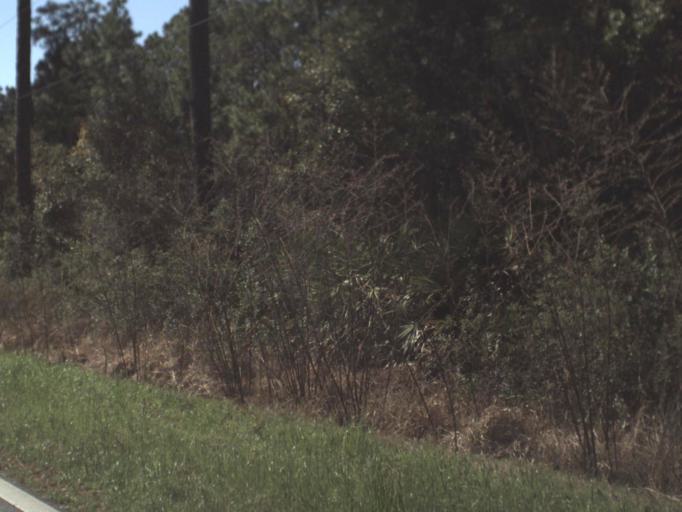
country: US
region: Florida
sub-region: Franklin County
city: Carrabelle
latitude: 29.8939
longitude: -84.5662
